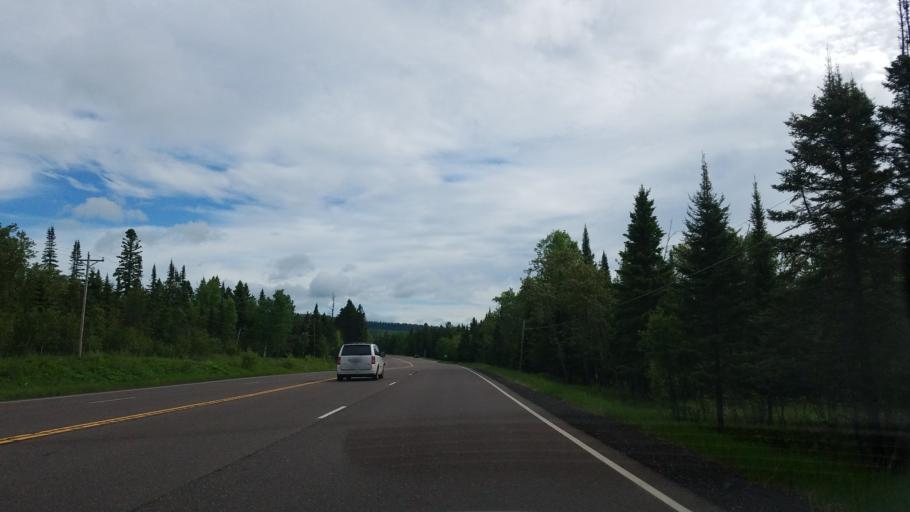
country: US
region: Minnesota
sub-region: Lake County
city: Two Harbors
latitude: 47.0834
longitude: -91.5822
